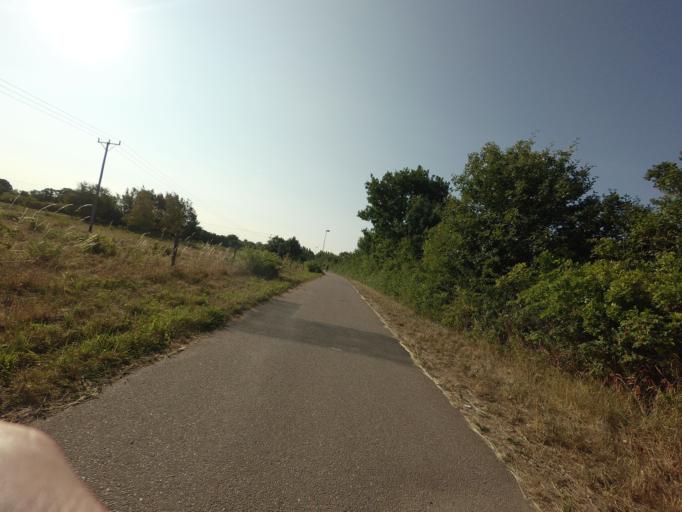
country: SE
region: Skane
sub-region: Landskrona
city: Asmundtorp
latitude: 55.8584
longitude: 12.8974
